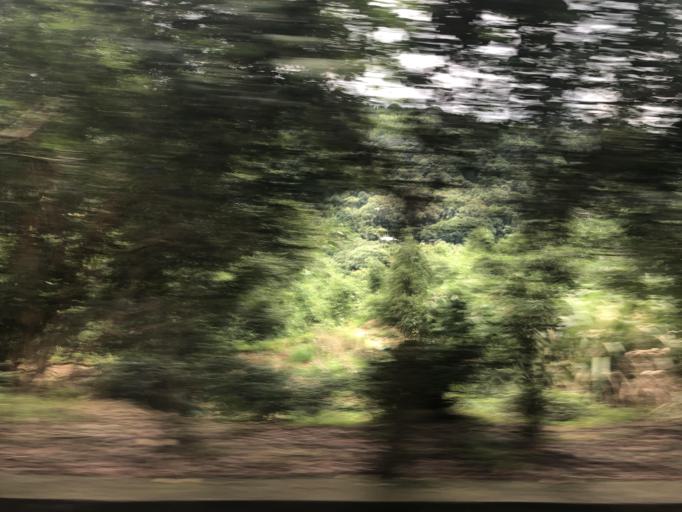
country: TW
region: Taiwan
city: Daxi
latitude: 24.8797
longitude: 121.4192
